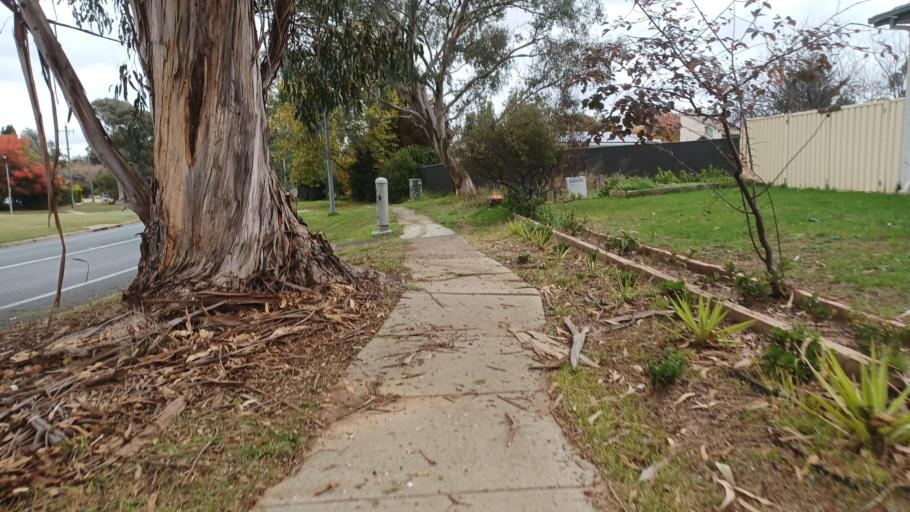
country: AU
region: Australian Capital Territory
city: Belconnen
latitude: -35.2028
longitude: 149.0403
